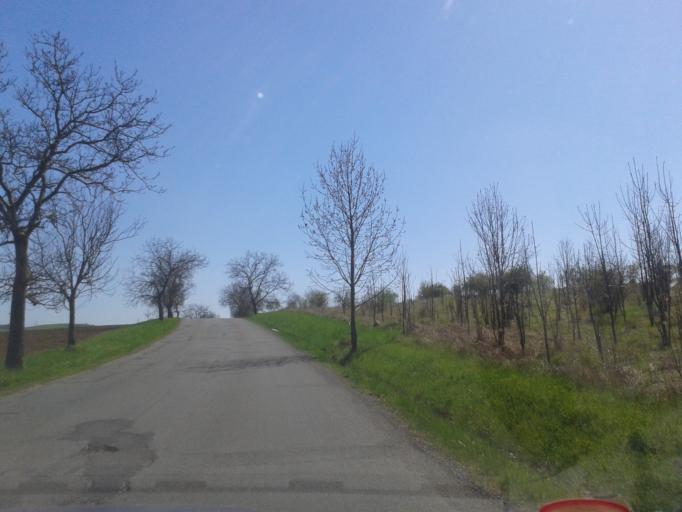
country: CZ
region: Central Bohemia
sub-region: Okres Beroun
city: Beroun
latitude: 49.9369
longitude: 14.0720
